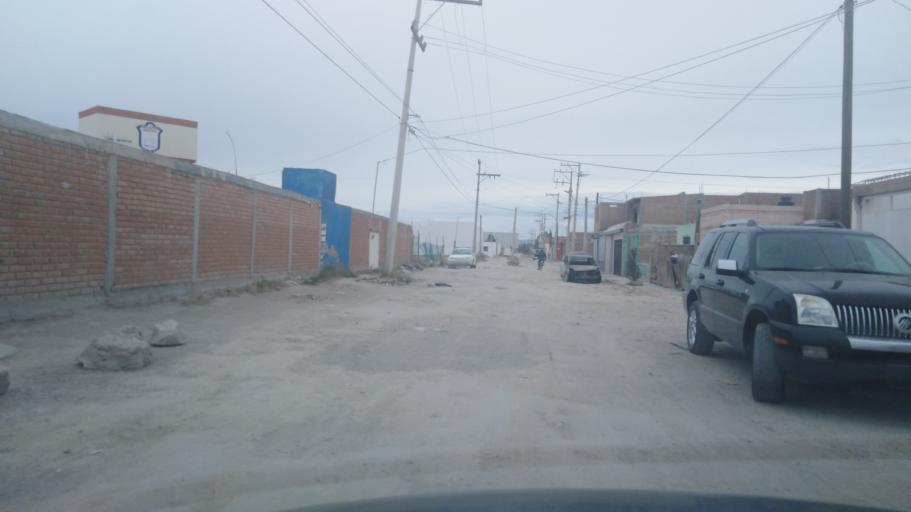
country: MX
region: Durango
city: Victoria de Durango
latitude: 24.0224
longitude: -104.6162
